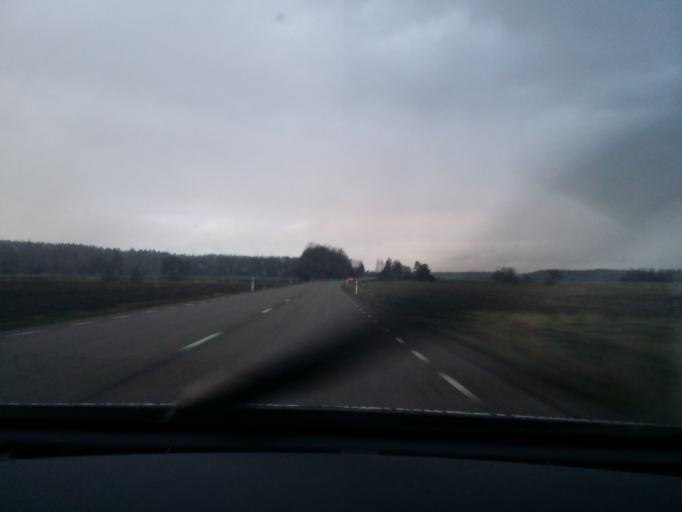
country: SE
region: Vaestmanland
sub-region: Hallstahammars Kommun
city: Kolback
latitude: 59.5451
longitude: 16.3297
